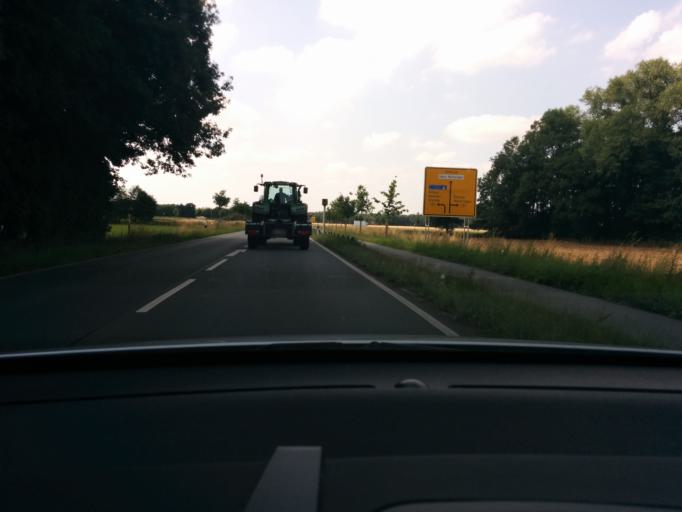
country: DE
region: North Rhine-Westphalia
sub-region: Regierungsbezirk Munster
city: Wettringen
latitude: 52.1781
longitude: 7.2782
